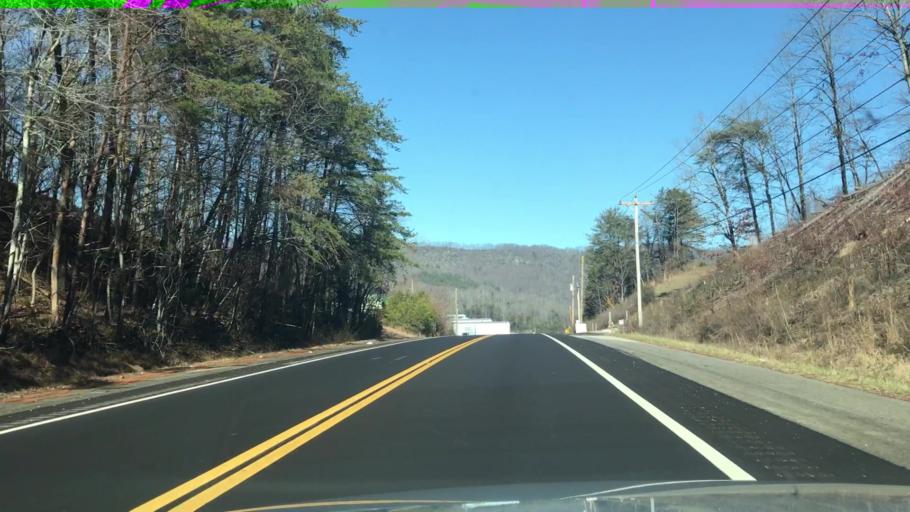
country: US
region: Tennessee
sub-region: Roane County
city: Midtown
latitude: 35.8912
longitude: -84.6177
